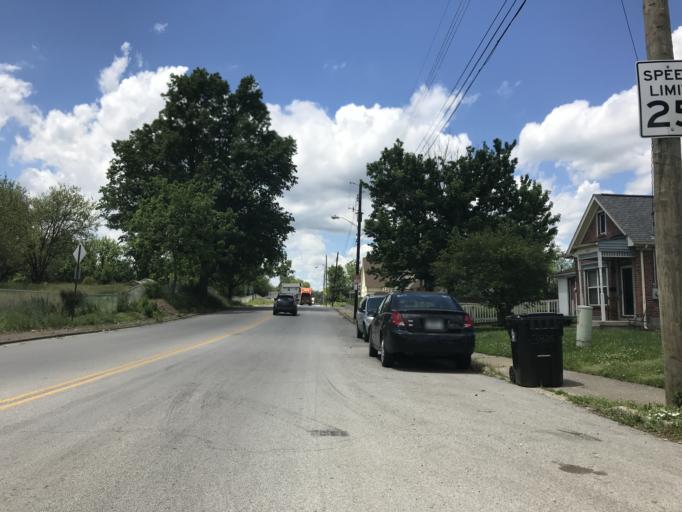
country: US
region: Kentucky
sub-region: Jefferson County
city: Shively
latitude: 38.2411
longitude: -85.8178
